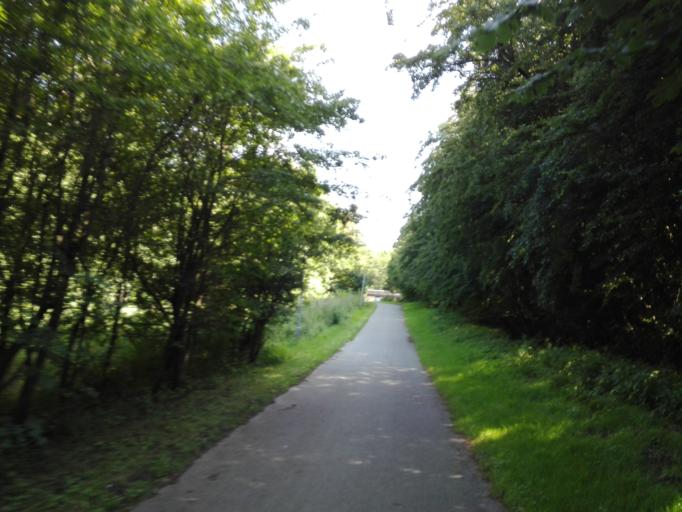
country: DK
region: Central Jutland
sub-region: Arhus Kommune
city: Tranbjerg
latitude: 56.1028
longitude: 10.1175
